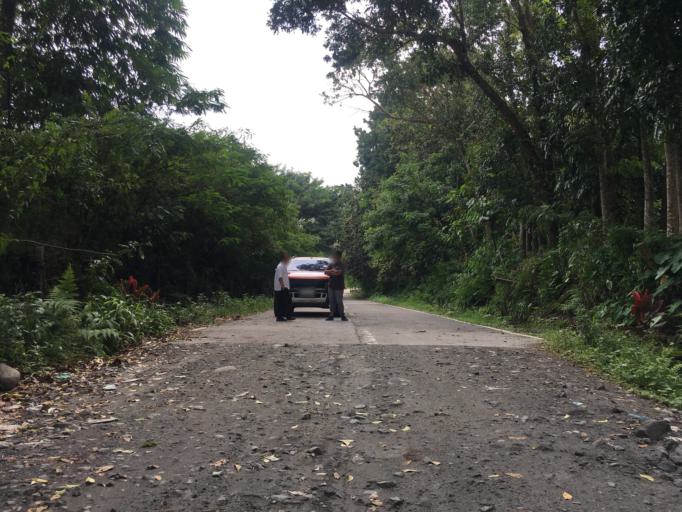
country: PH
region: Western Visayas
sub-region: Province of Negros Occidental
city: Alegria
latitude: 10.6512
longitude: 123.1043
